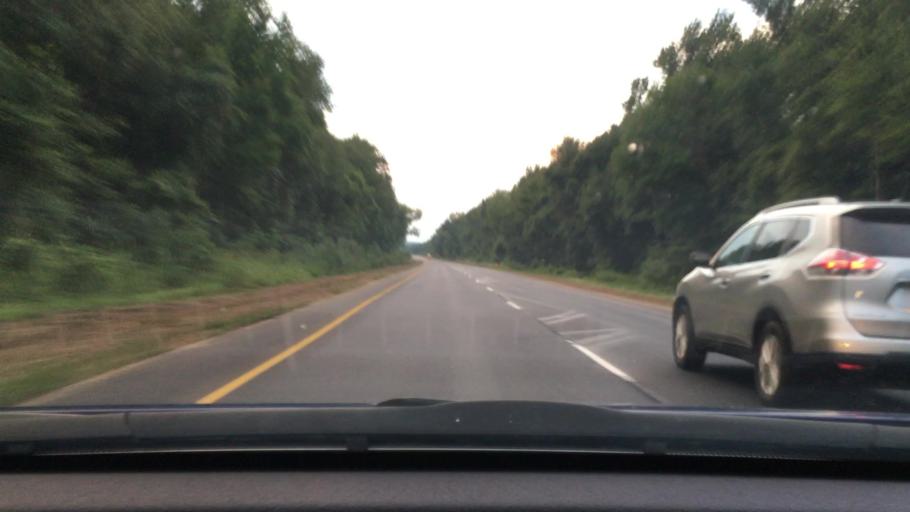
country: US
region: South Carolina
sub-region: Sumter County
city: Stateburg
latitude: 33.9490
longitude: -80.6173
